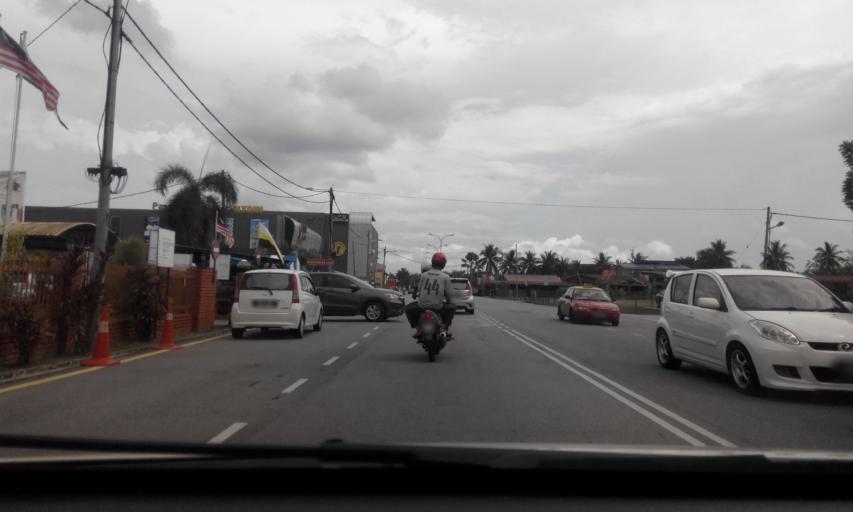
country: MY
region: Perak
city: Parit Buntar
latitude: 5.1302
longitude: 100.4819
